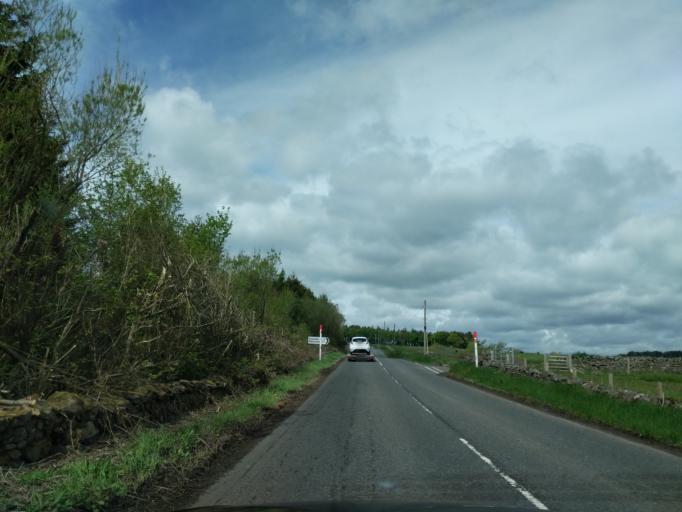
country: GB
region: Scotland
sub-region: The Scottish Borders
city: Earlston
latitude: 55.6934
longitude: -2.5750
